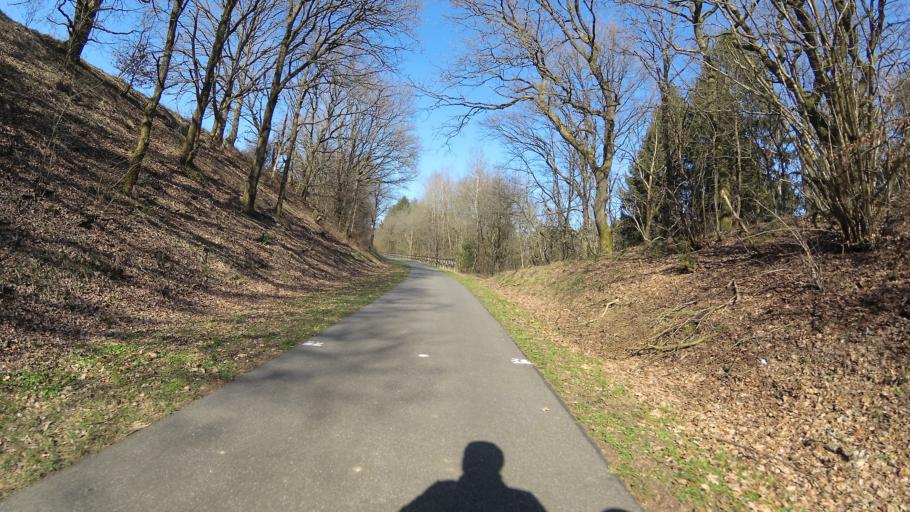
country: DE
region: Rheinland-Pfalz
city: Reinsfeld
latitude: 49.6655
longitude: 6.8694
